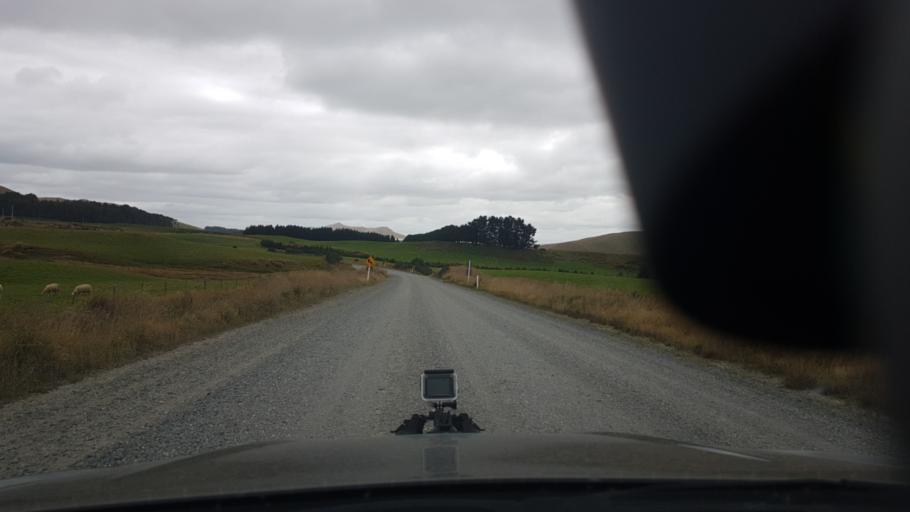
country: NZ
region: Otago
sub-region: Clutha District
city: Papatowai
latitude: -46.3208
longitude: 169.3713
